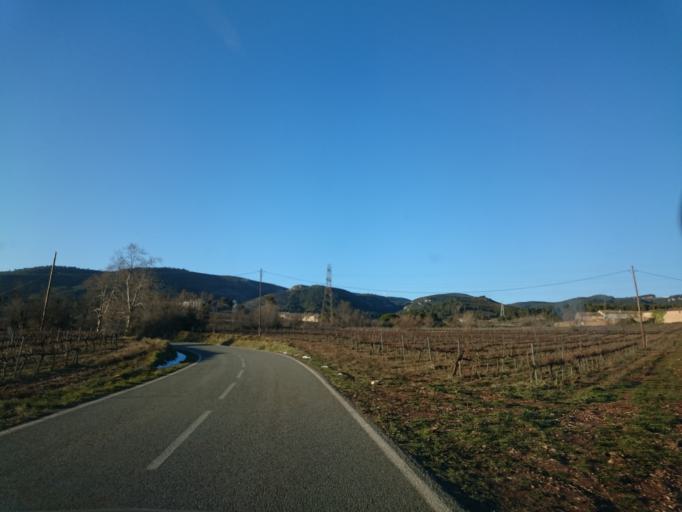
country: ES
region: Catalonia
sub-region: Provincia de Tarragona
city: la Bisbal del Penedes
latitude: 41.3707
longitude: 1.5001
